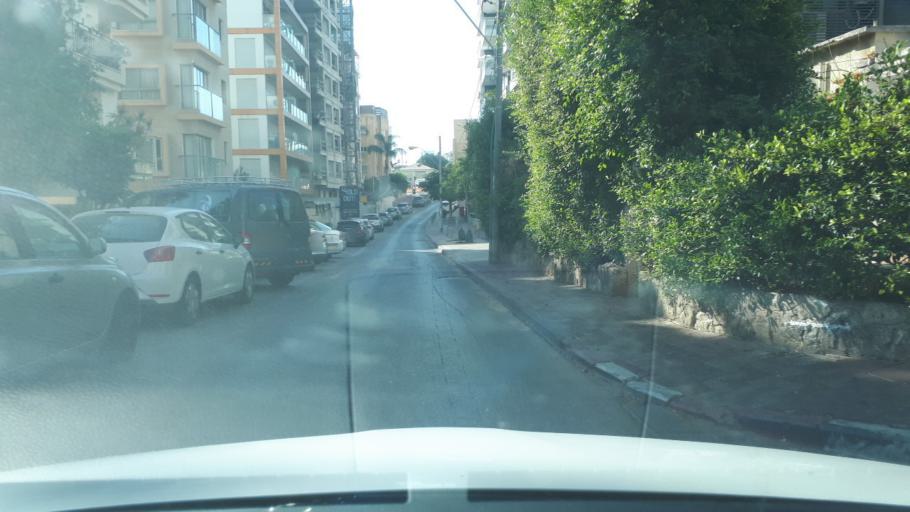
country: IL
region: Tel Aviv
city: Giv`atayim
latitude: 32.0674
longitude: 34.8231
